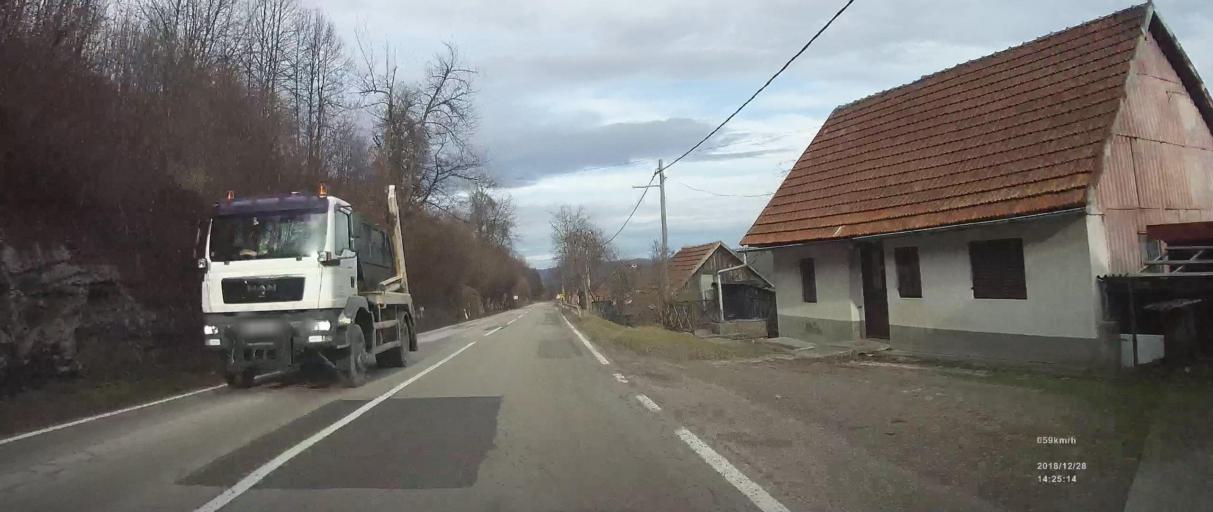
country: HR
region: Primorsko-Goranska
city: Vrbovsko
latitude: 45.3922
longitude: 15.1054
